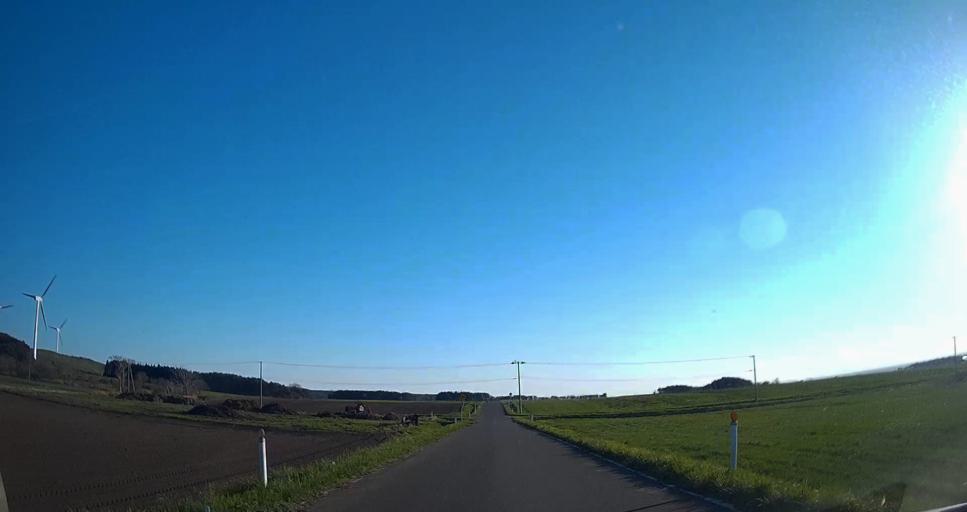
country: JP
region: Aomori
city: Mutsu
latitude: 41.1199
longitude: 141.2785
